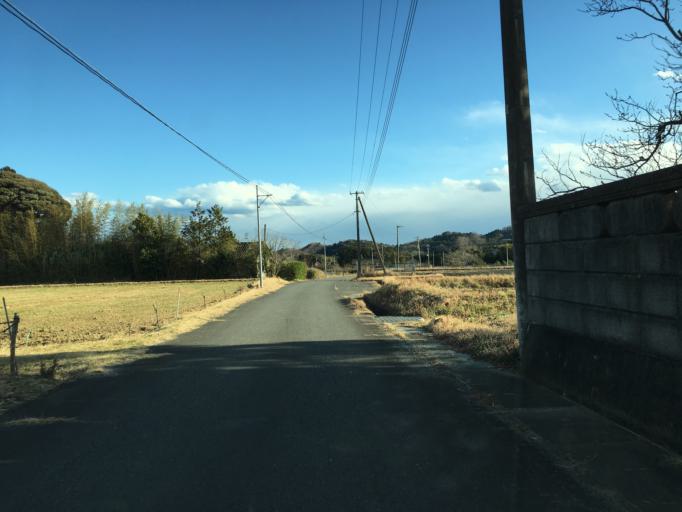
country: JP
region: Fukushima
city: Iwaki
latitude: 37.1190
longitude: 140.8971
